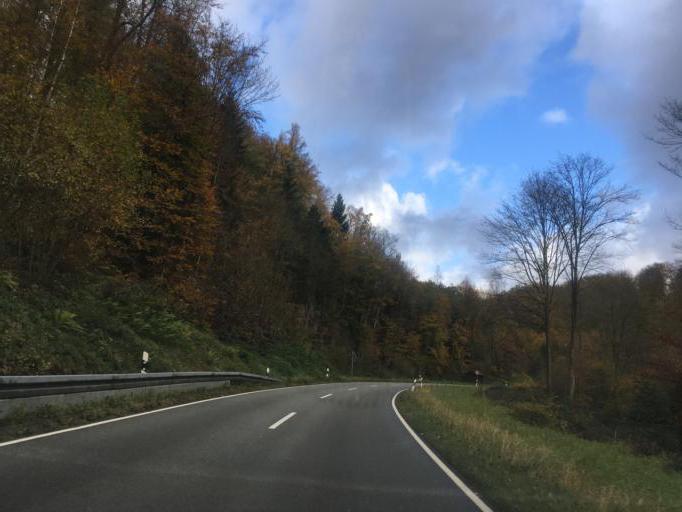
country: DE
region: Lower Saxony
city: Furstenberg
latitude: 51.7451
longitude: 9.4290
